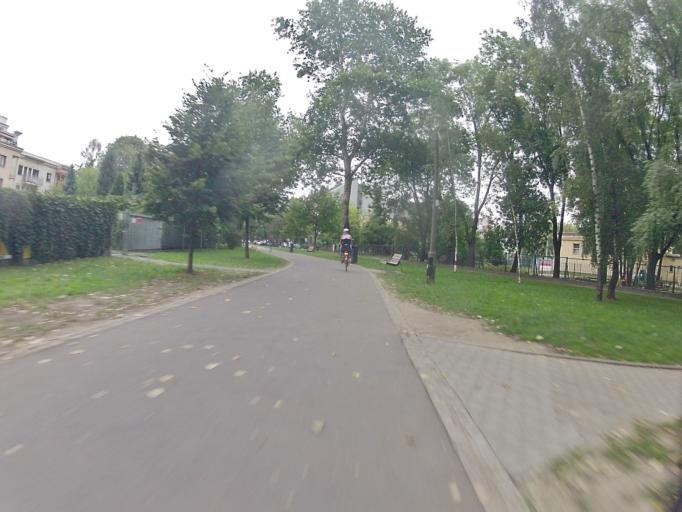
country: PL
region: Lesser Poland Voivodeship
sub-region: Krakow
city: Krakow
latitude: 50.0748
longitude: 19.9215
